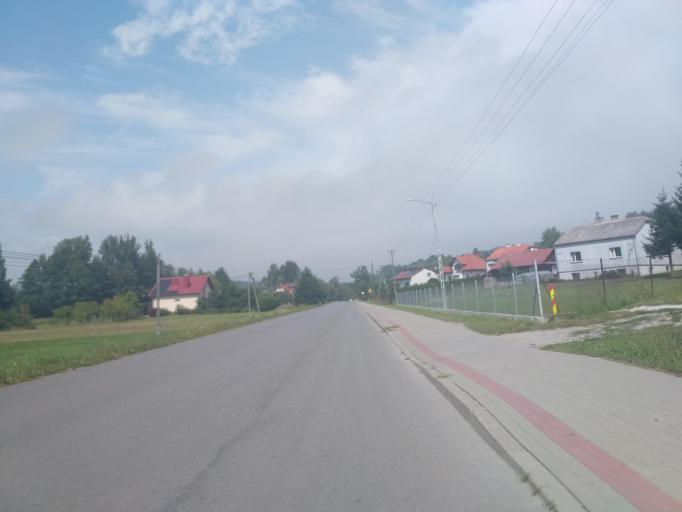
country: PL
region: Subcarpathian Voivodeship
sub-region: Powiat rzeszowski
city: Chmielnik
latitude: 49.9871
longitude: 22.1120
